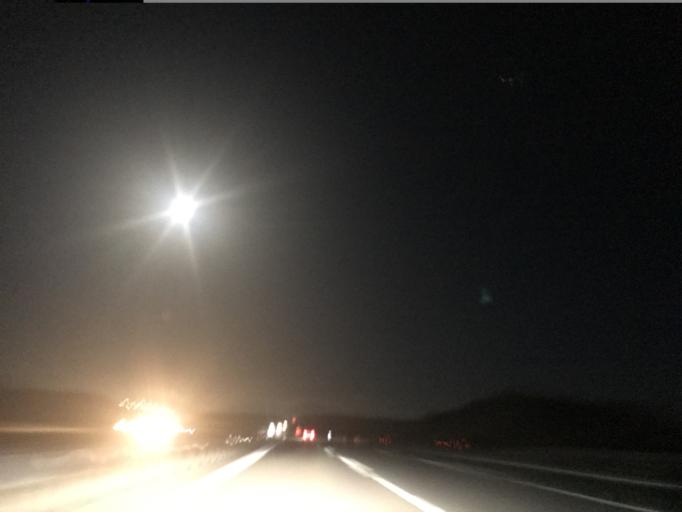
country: TR
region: Nigde
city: Ulukisla
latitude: 37.6401
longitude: 34.3853
